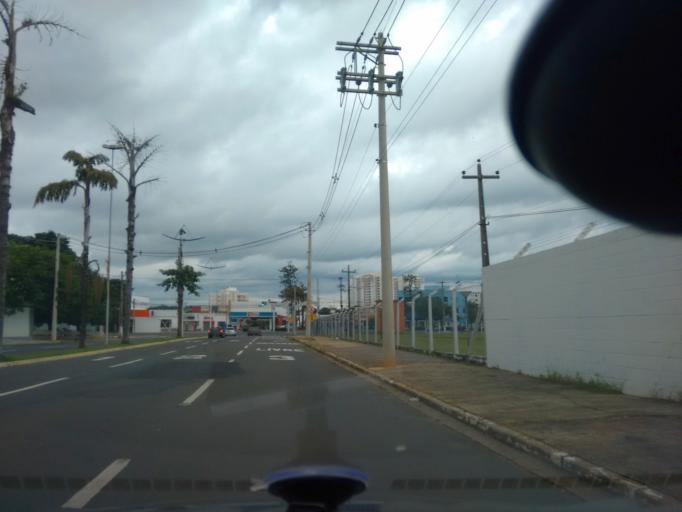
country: BR
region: Sao Paulo
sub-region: Indaiatuba
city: Indaiatuba
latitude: -23.0871
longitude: -47.1988
